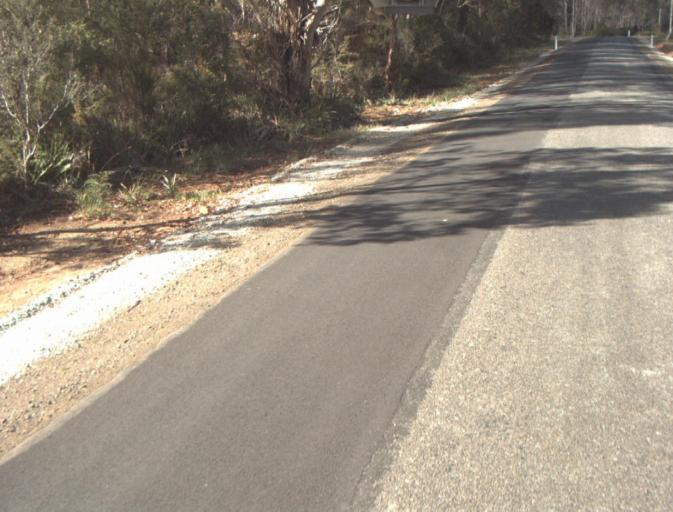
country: AU
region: Tasmania
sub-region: Launceston
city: Mayfield
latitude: -41.3105
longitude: 147.1986
